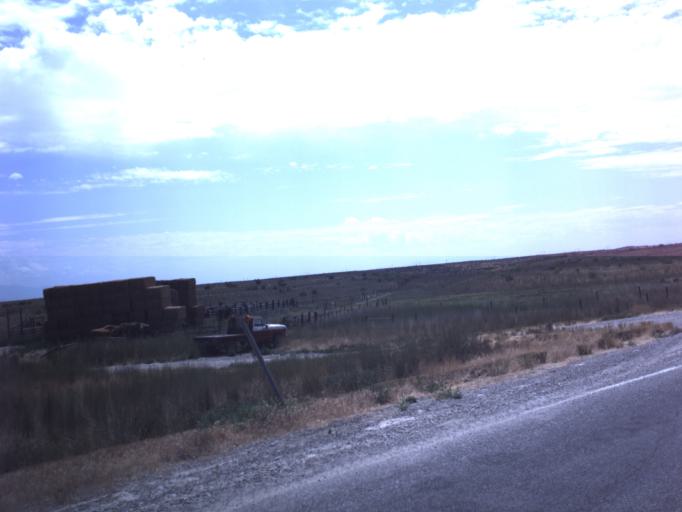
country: US
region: Utah
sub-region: Box Elder County
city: Tremonton
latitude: 41.6374
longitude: -112.3141
